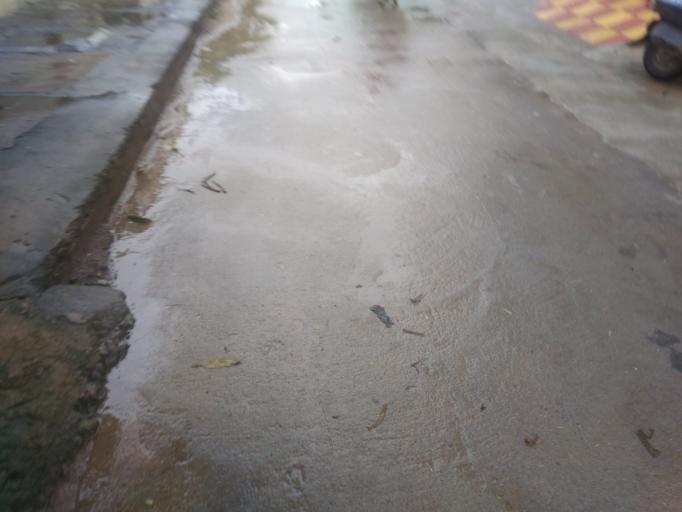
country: IN
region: Telangana
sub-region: Rangareddi
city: Secunderabad
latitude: 17.5110
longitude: 78.5086
